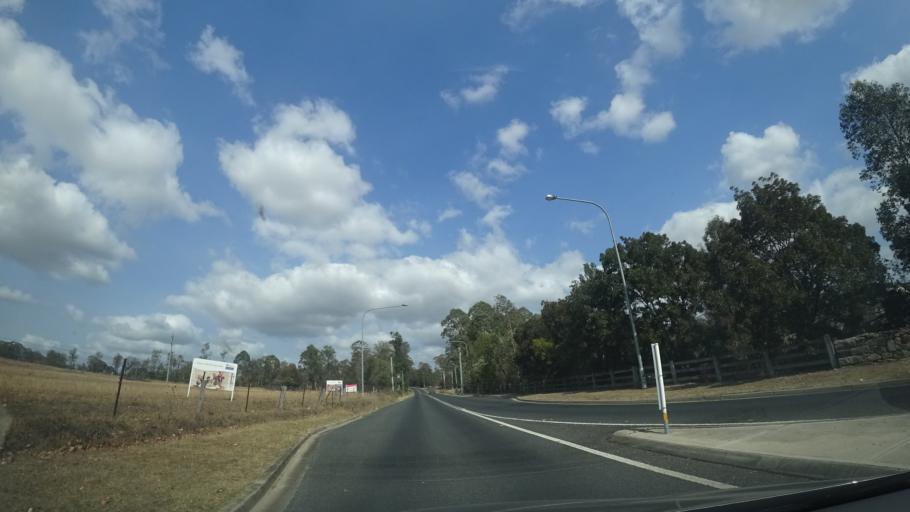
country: AU
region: New South Wales
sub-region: Wollondilly
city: Picton
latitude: -34.1859
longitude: 150.5866
